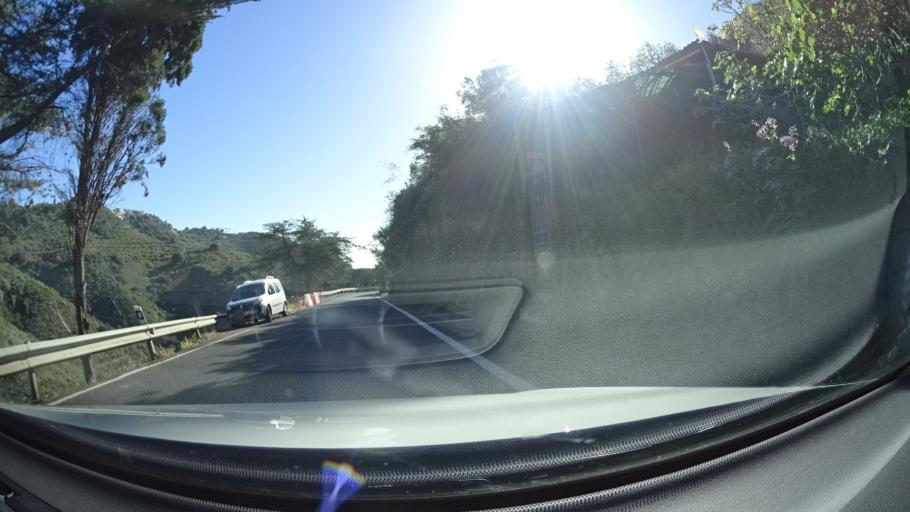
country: ES
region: Canary Islands
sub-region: Provincia de Las Palmas
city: Santa Brigida
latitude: 28.0248
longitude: -15.4732
